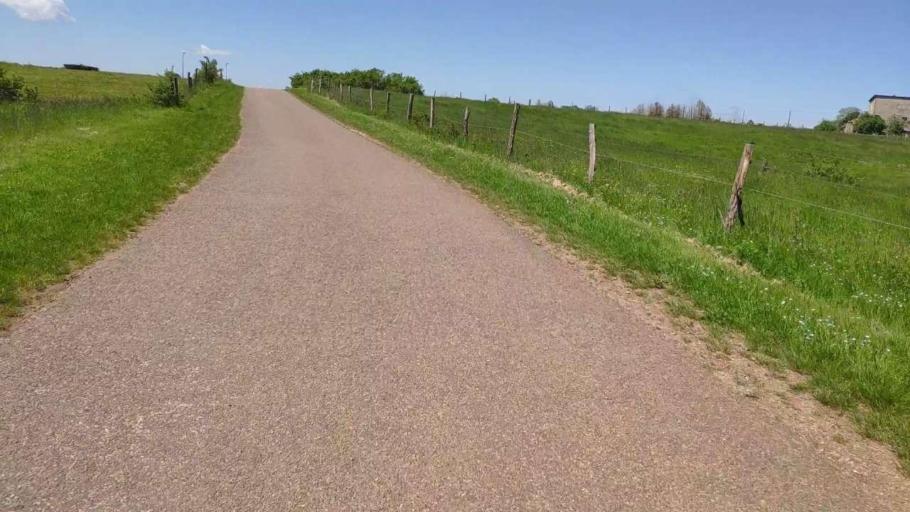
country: FR
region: Franche-Comte
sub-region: Departement du Jura
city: Poligny
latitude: 46.7356
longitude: 5.7117
